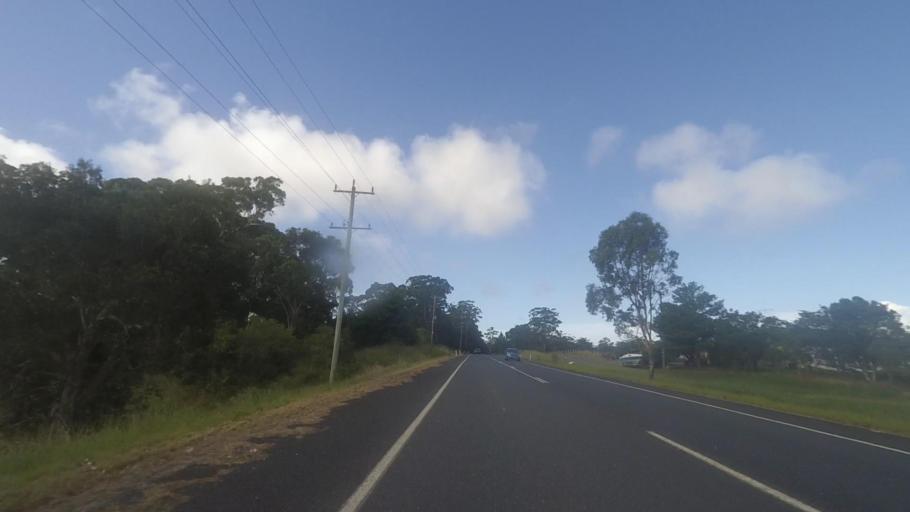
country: AU
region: New South Wales
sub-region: Great Lakes
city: Forster
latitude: -32.3590
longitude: 152.5037
